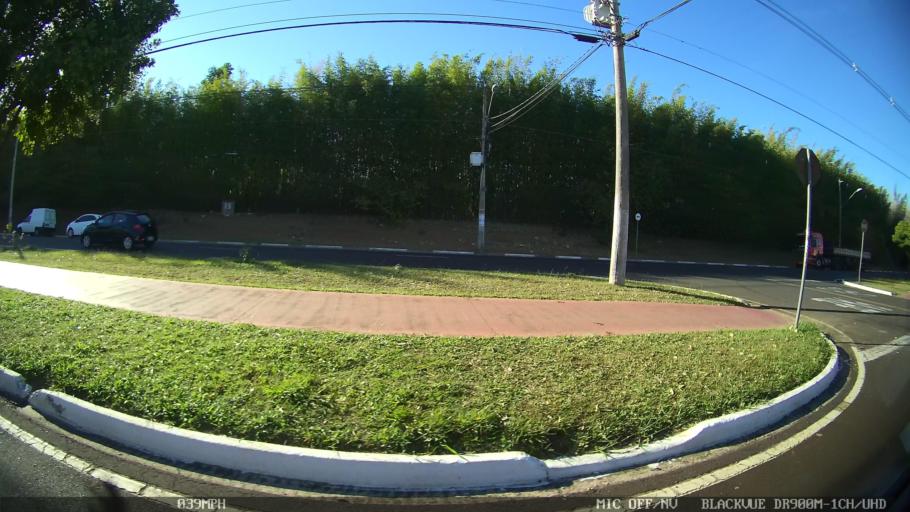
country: BR
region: Sao Paulo
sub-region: Franca
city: Franca
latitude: -20.5690
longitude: -47.3665
